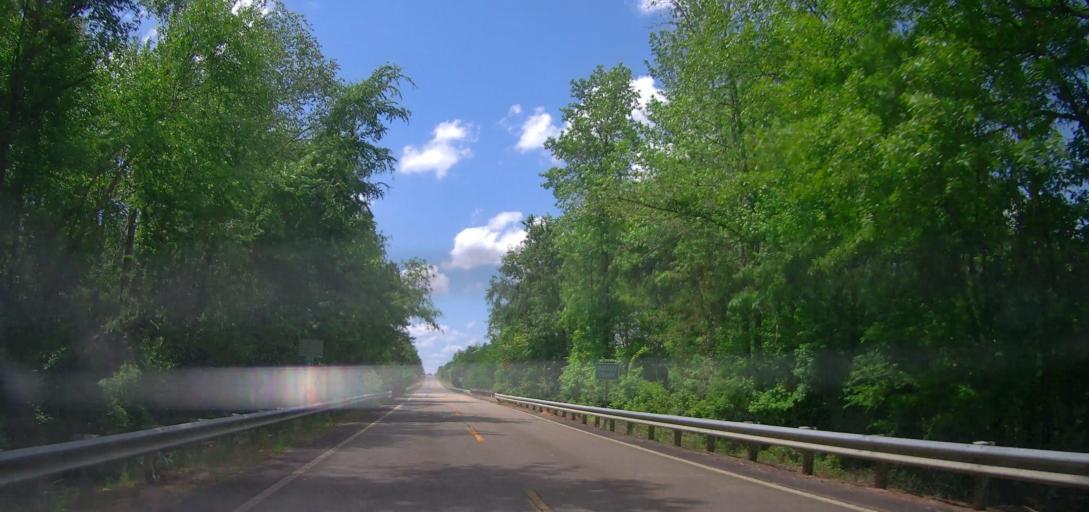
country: US
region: Georgia
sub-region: Dodge County
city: Chester
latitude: 32.5354
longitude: -83.1990
